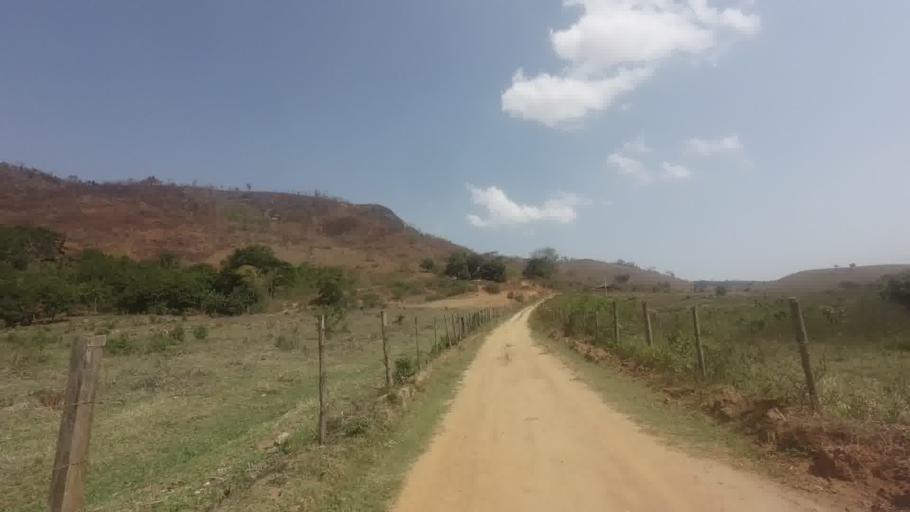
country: BR
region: Espirito Santo
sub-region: Sao Jose Do Calcado
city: Sao Jose do Calcado
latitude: -21.0287
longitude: -41.5170
